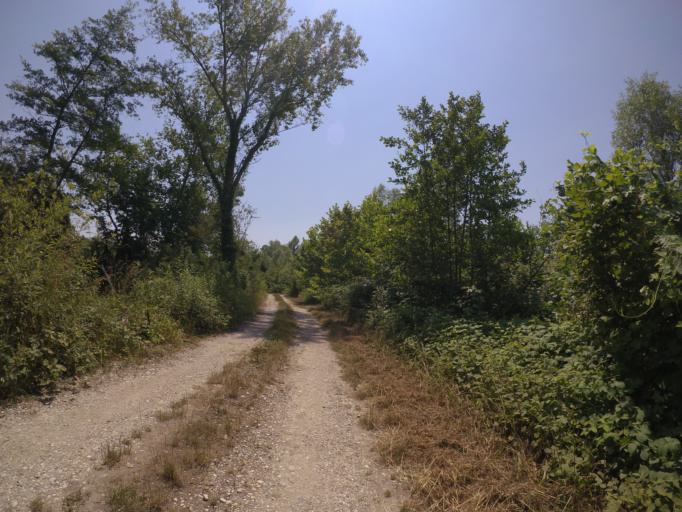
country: IT
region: Friuli Venezia Giulia
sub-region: Provincia di Udine
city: Rivignano
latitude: 45.9015
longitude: 13.0362
